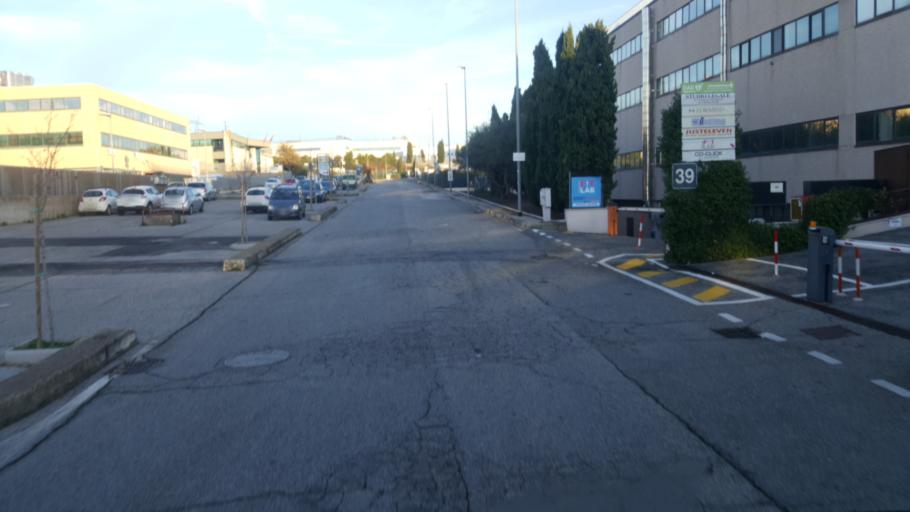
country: IT
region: Latium
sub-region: Citta metropolitana di Roma Capitale
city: Formello
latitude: 42.0512
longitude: 12.4001
